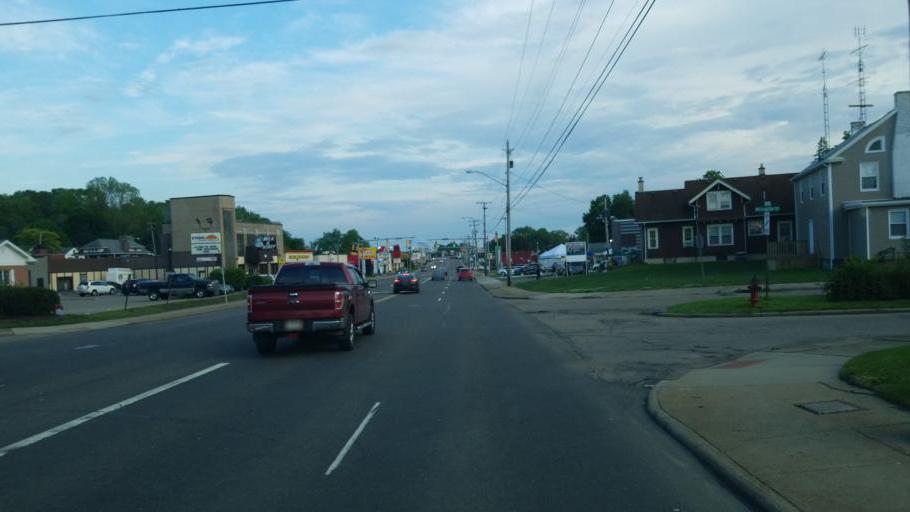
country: US
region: Ohio
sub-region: Stark County
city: Canton
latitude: 40.8373
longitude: -81.3898
